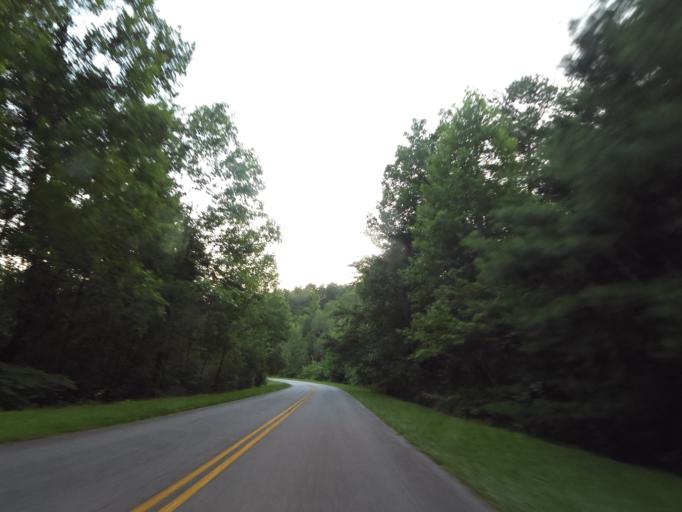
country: US
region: Tennessee
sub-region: Blount County
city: Maryville
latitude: 35.5810
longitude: -84.0002
